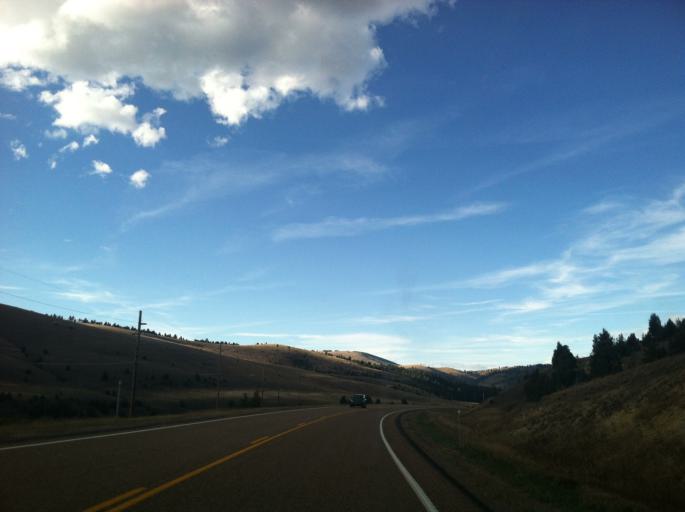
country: US
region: Montana
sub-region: Granite County
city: Philipsburg
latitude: 46.3811
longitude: -113.3132
